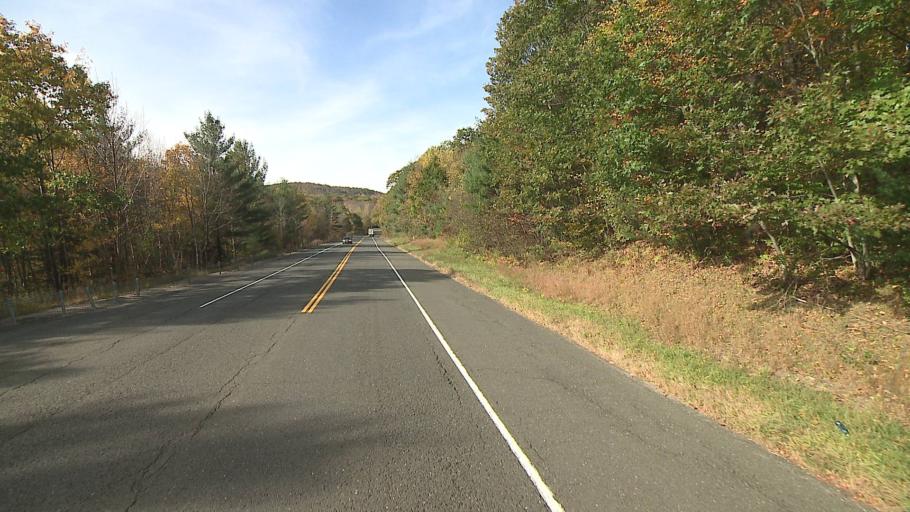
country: US
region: Connecticut
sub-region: Litchfield County
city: Winchester Center
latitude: 41.9416
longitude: -73.1096
